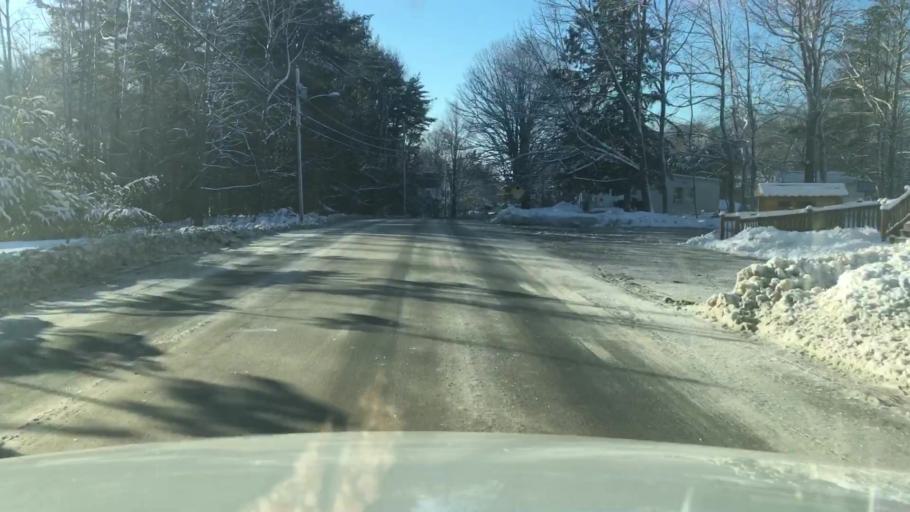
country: US
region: Maine
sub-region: Kennebec County
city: Readfield
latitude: 44.4160
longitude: -69.9168
